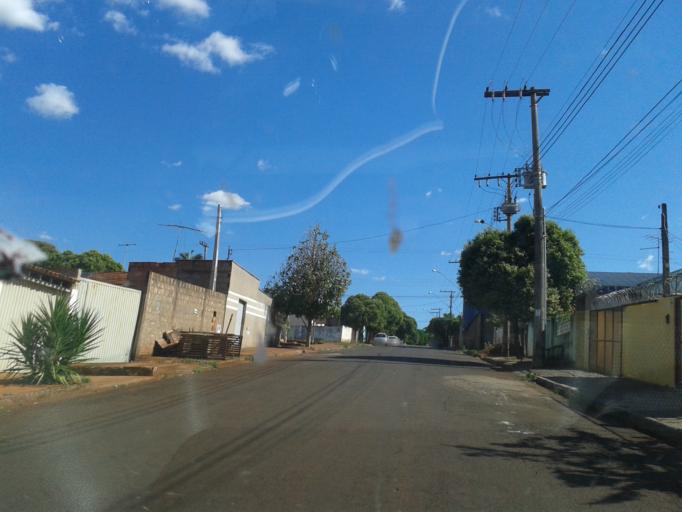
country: BR
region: Minas Gerais
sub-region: Ituiutaba
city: Ituiutaba
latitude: -18.9505
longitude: -49.4594
